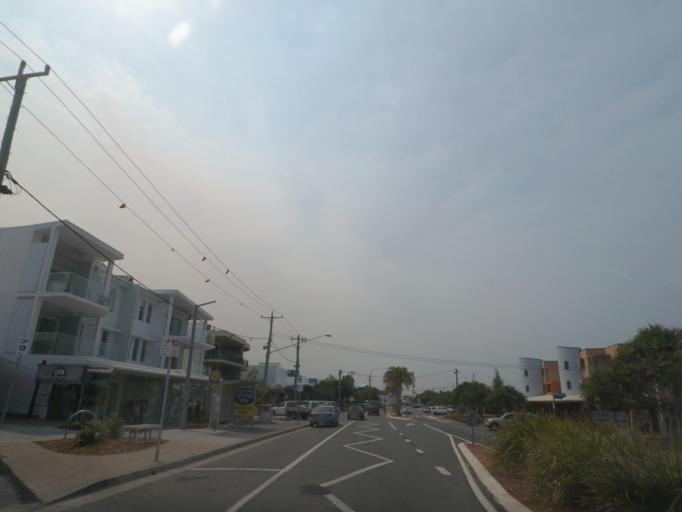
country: AU
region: New South Wales
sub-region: Tweed
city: Casuarina
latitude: -28.3325
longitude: 153.5699
